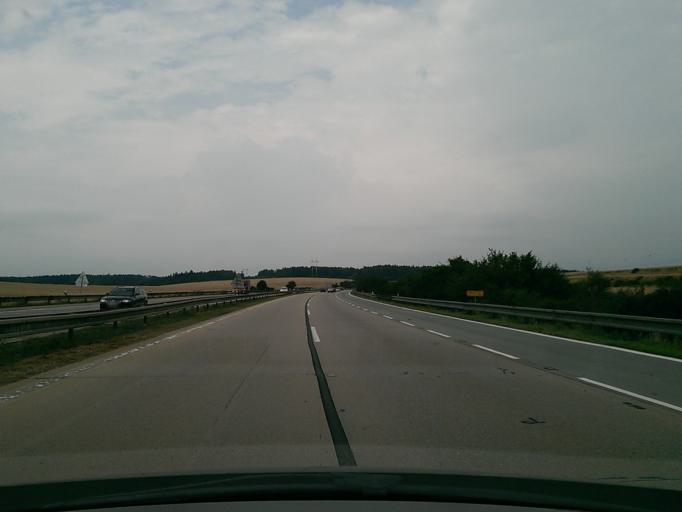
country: CZ
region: South Moravian
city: Ricany
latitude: 49.2219
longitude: 16.3961
